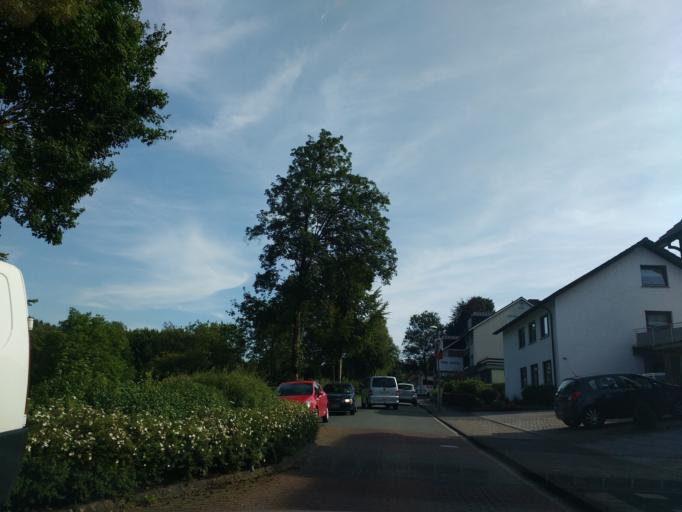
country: DE
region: North Rhine-Westphalia
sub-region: Regierungsbezirk Detmold
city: Wunnenberg
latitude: 51.5158
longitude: 8.7009
